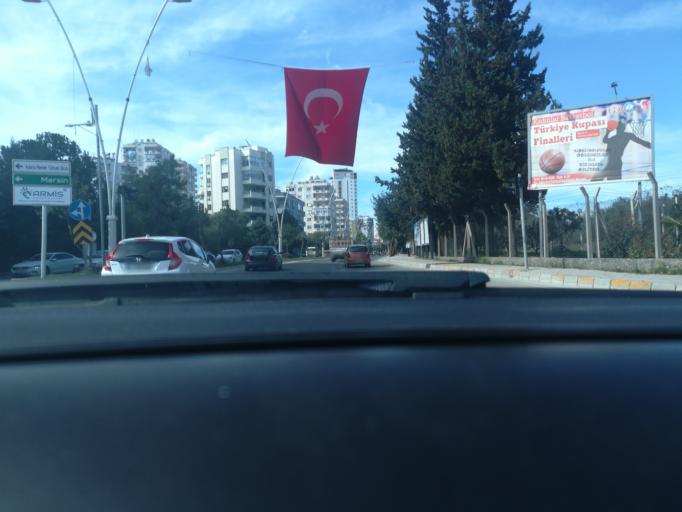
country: TR
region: Adana
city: Adana
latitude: 37.0312
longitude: 35.3234
